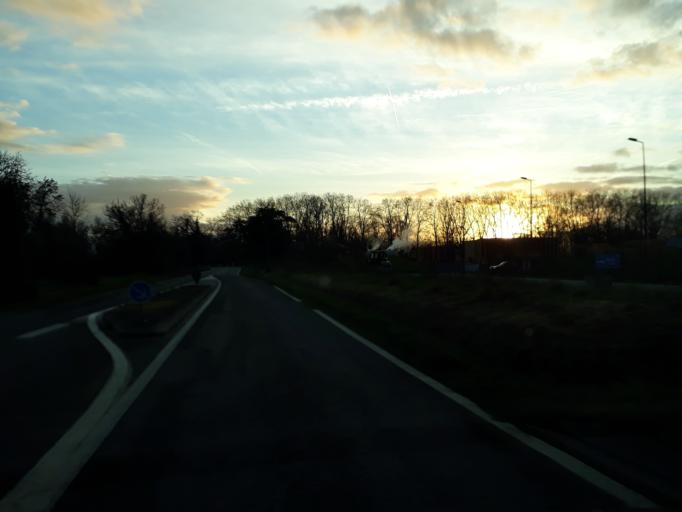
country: FR
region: Midi-Pyrenees
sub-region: Departement de la Haute-Garonne
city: Longages
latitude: 43.3390
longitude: 1.2545
